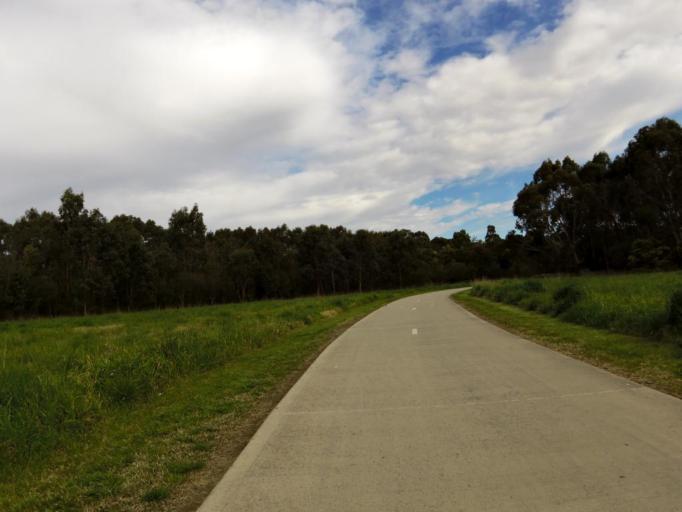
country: AU
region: Victoria
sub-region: Knox
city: Wantirna
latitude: -37.8541
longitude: 145.2122
